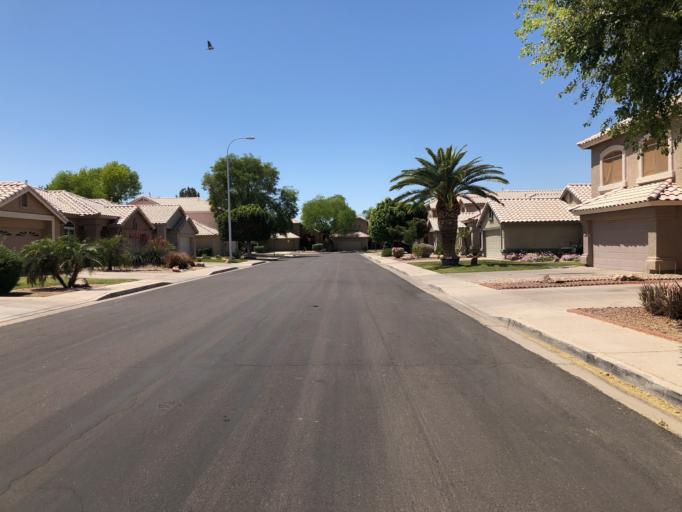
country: US
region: Arizona
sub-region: Maricopa County
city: Guadalupe
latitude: 33.3189
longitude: -111.9311
